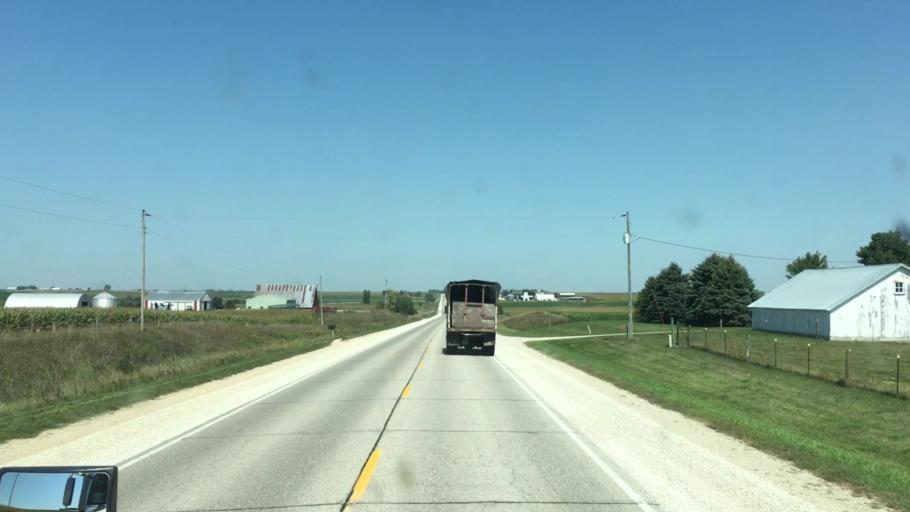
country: US
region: Iowa
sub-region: Tama County
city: Dysart
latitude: 42.0615
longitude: -92.2988
